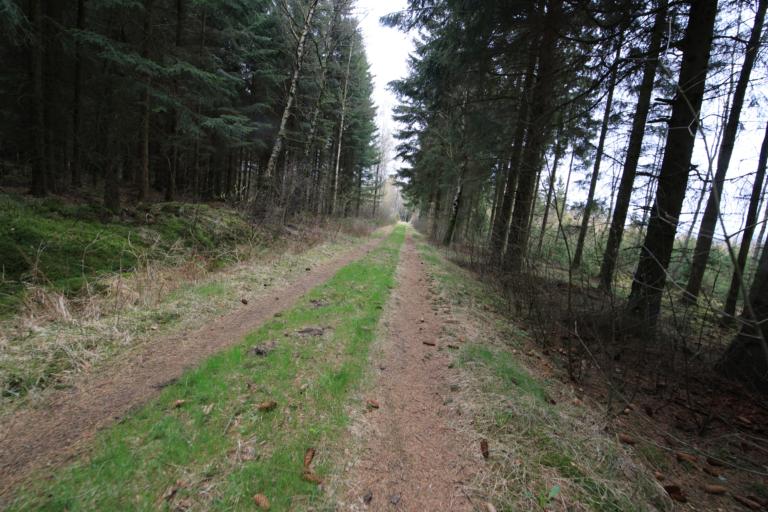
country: SE
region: Halland
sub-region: Varbergs Kommun
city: Tvaaker
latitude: 57.1524
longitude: 12.4578
